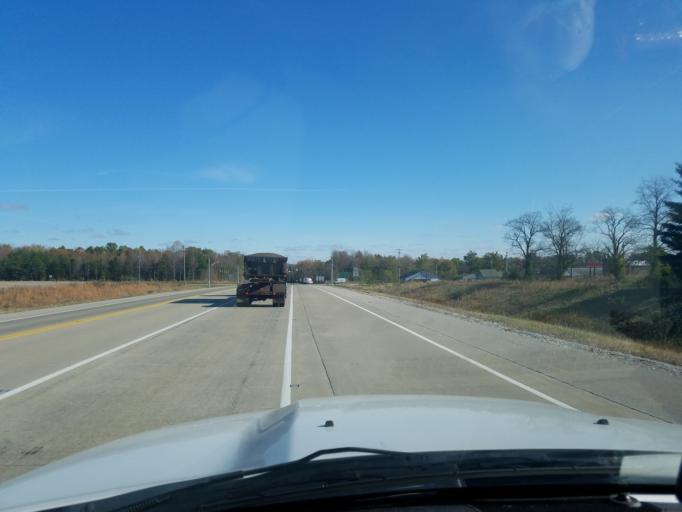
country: US
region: Indiana
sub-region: Jennings County
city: North Vernon
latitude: 39.0231
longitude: -85.6530
